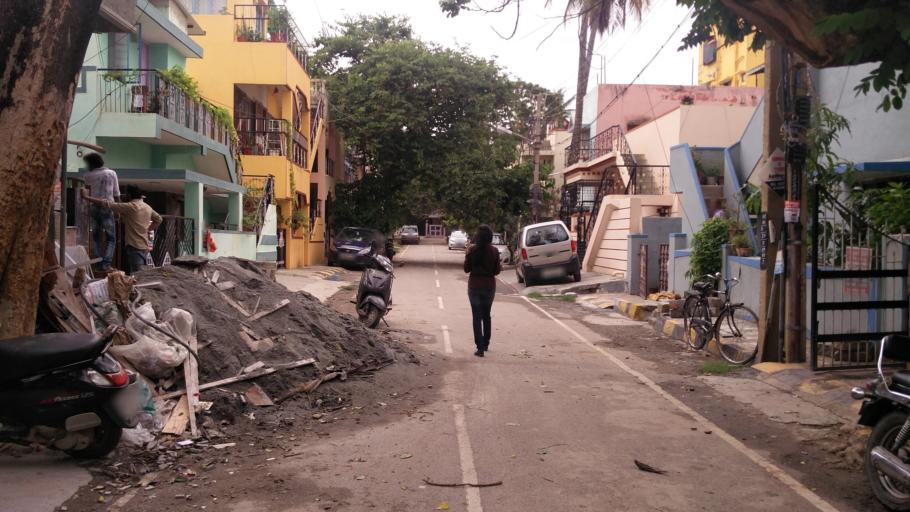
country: IN
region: Karnataka
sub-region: Bangalore Urban
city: Bangalore
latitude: 12.9773
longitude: 77.6346
